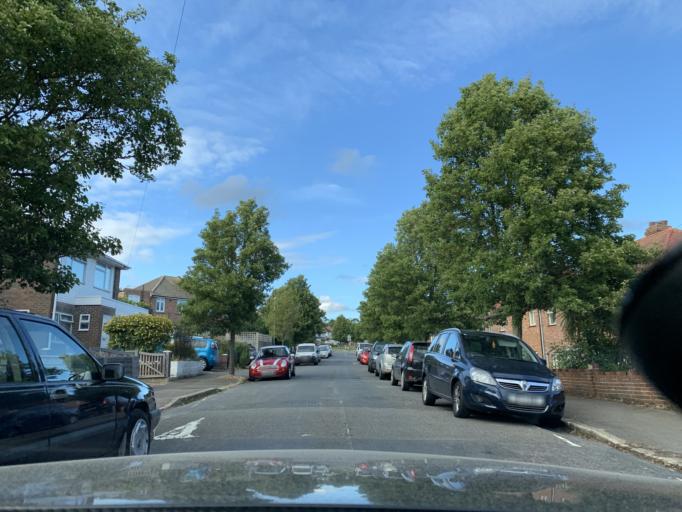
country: GB
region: England
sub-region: East Sussex
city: Saint Leonards-on-Sea
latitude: 50.8748
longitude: 0.5534
